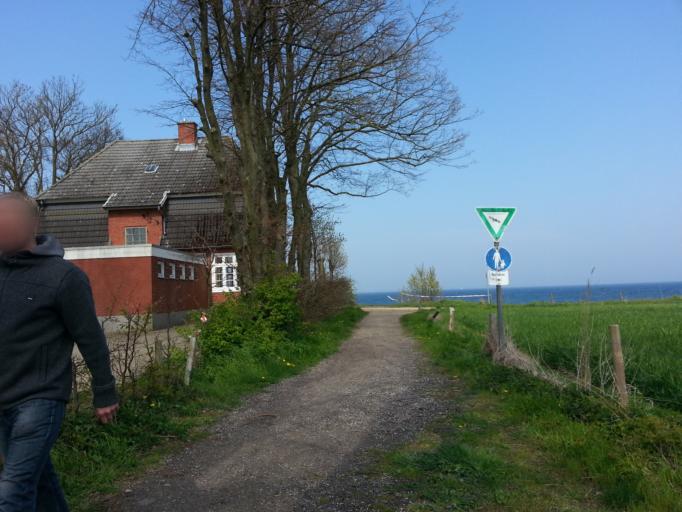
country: DE
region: Schleswig-Holstein
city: Travemuende
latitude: 53.9929
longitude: 10.8570
